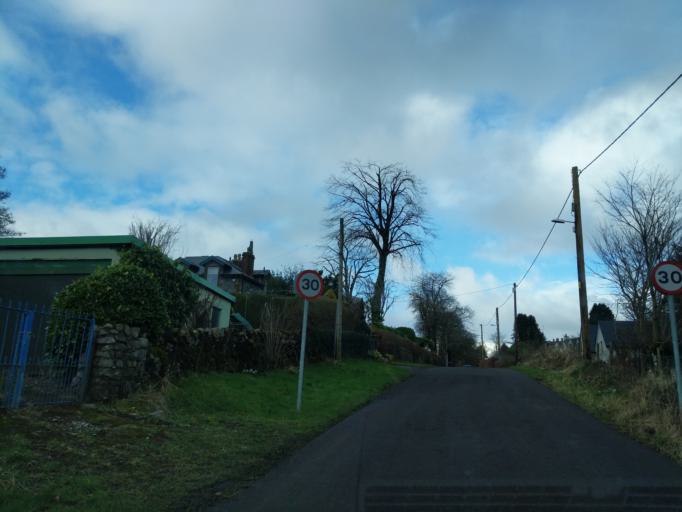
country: GB
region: Scotland
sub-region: Dumfries and Galloway
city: Moffat
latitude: 55.3235
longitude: -3.4308
